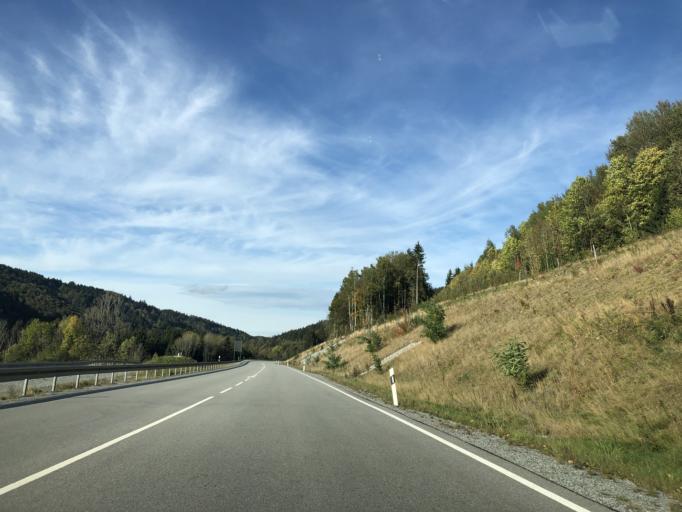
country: DE
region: Bavaria
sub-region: Lower Bavaria
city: Grafling
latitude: 48.9229
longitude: 12.9804
